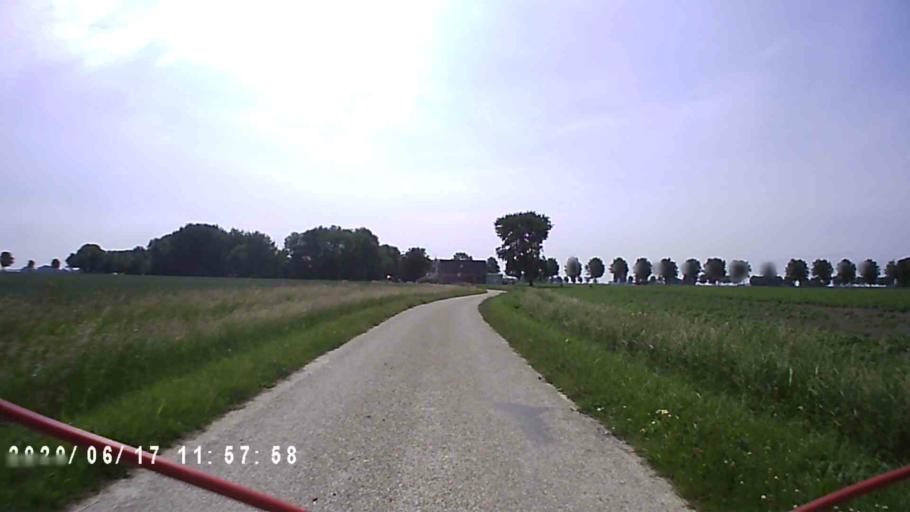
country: NL
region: Groningen
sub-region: Gemeente De Marne
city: Ulrum
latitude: 53.3453
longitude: 6.3265
